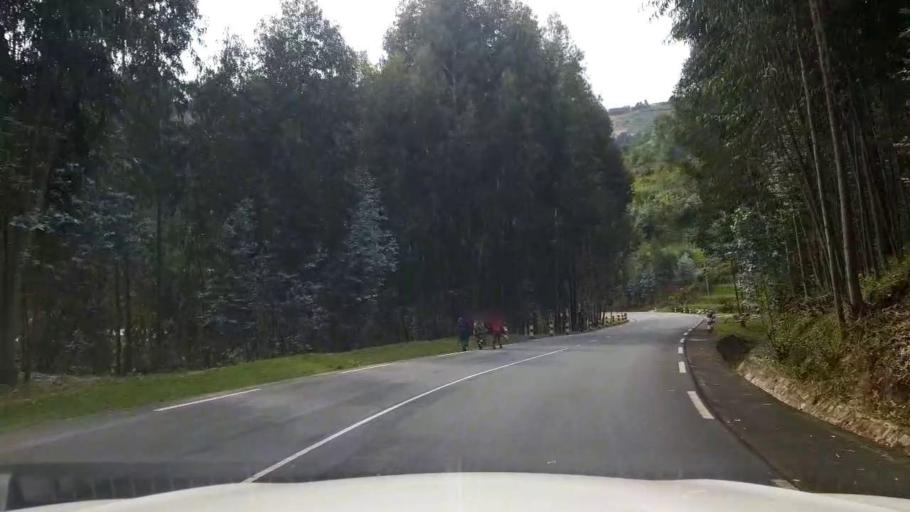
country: RW
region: Northern Province
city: Musanze
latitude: -1.6784
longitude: 29.5170
